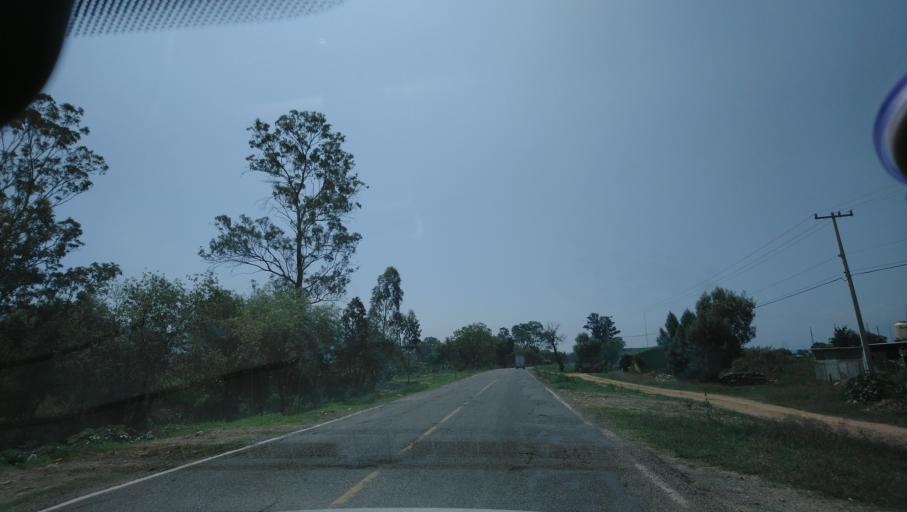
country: MX
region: Oaxaca
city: Santa Maria del Tule
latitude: 17.0431
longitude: -96.6286
